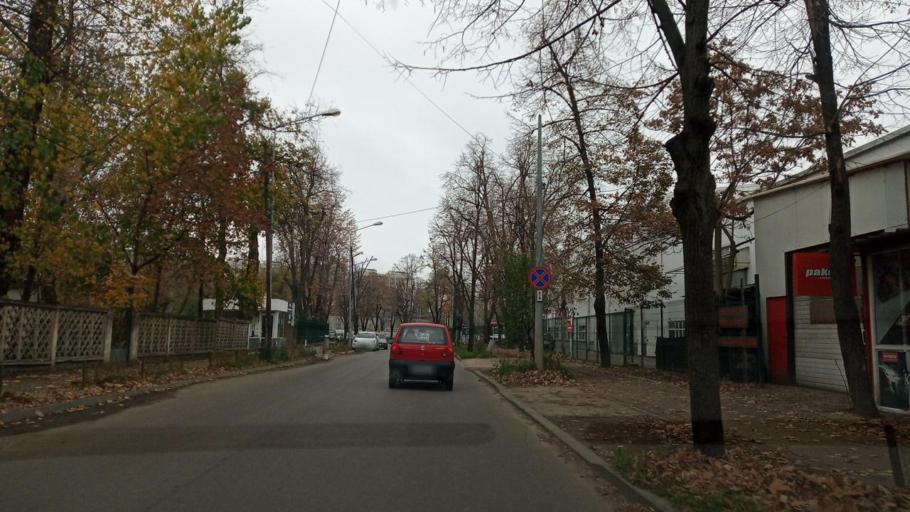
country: RO
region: Ilfov
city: Dobroesti
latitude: 44.4363
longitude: 26.1793
